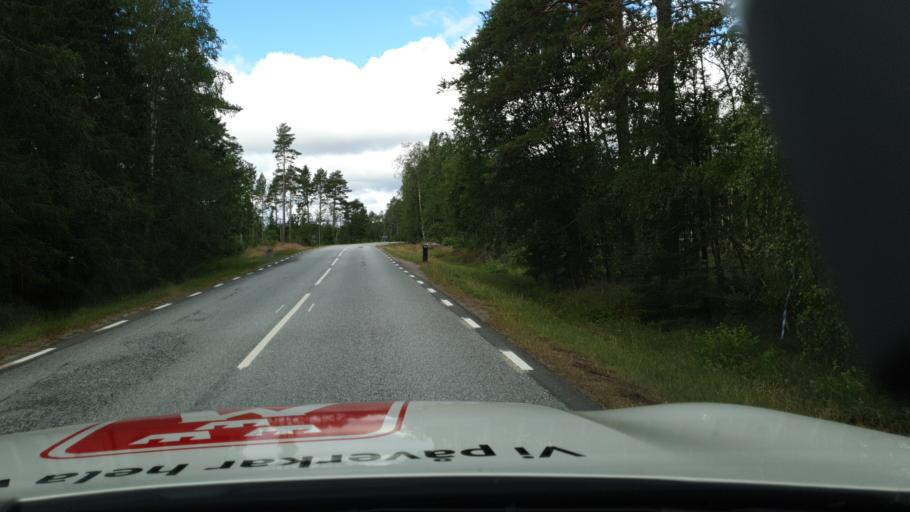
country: SE
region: Vaesterbotten
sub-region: Umea Kommun
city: Roback
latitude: 63.6761
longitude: 20.1466
